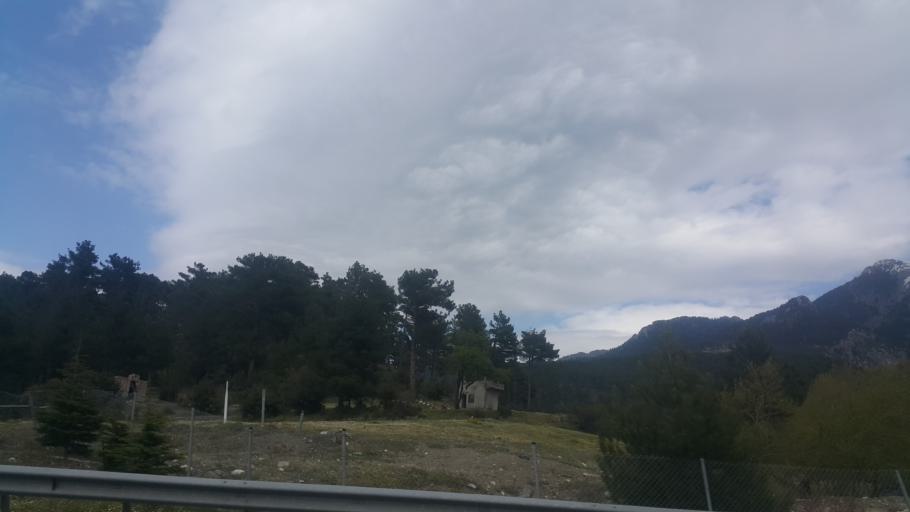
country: TR
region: Adana
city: Pozanti
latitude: 37.4144
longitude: 34.8809
